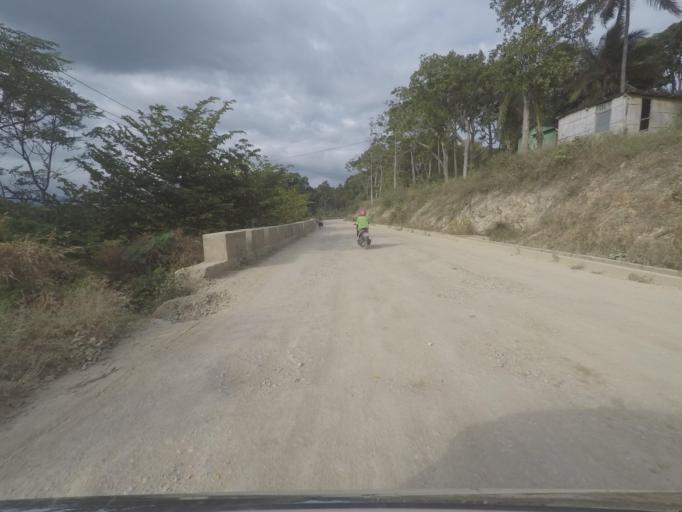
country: TL
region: Baucau
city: Venilale
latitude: -8.5869
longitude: 126.3877
